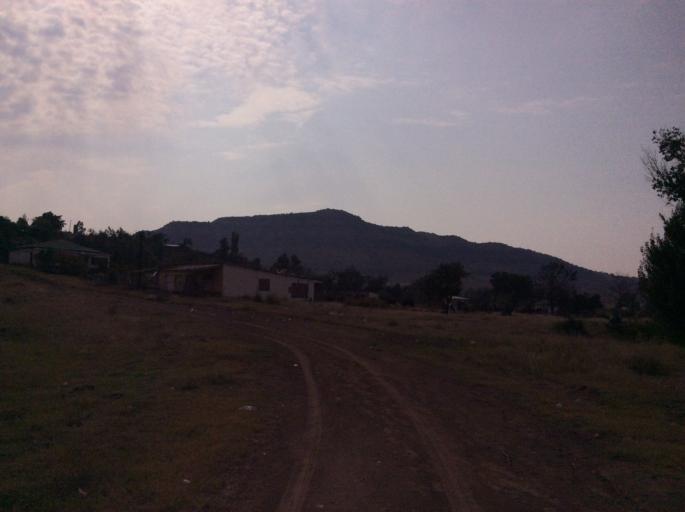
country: LS
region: Mafeteng
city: Mafeteng
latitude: -29.7262
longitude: 27.0322
